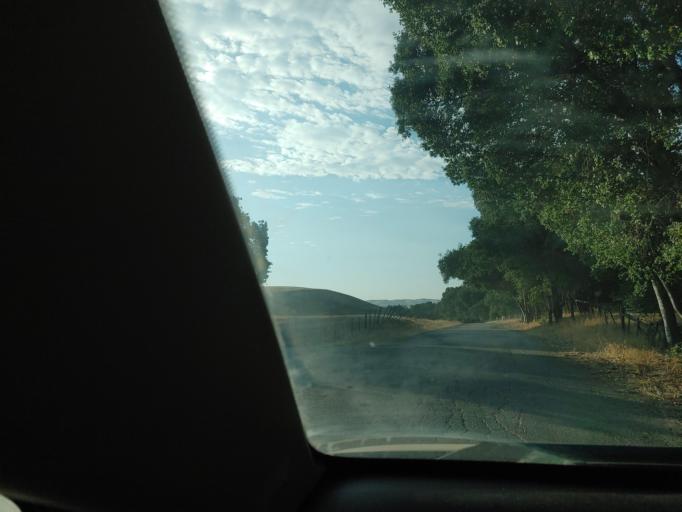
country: US
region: California
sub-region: San Benito County
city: Ridgemark
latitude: 36.7968
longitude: -121.2645
